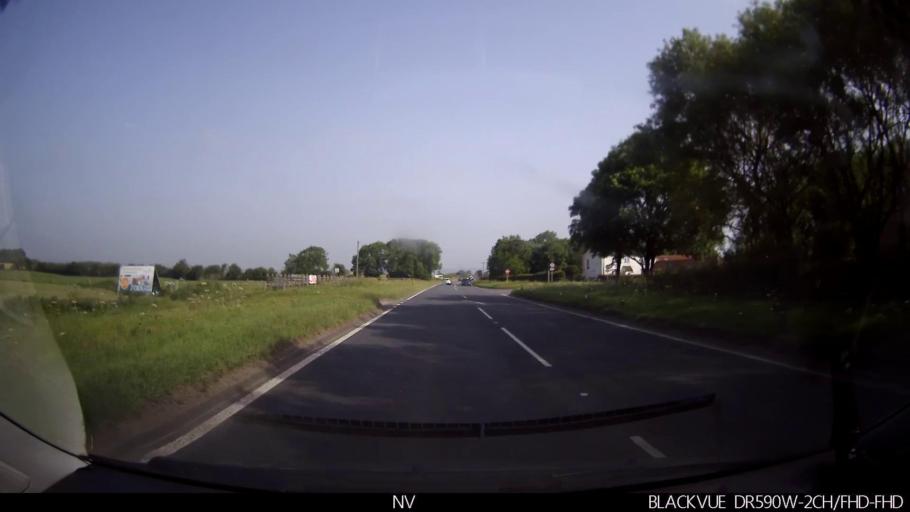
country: GB
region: England
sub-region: North Yorkshire
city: East Ayton
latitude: 54.2152
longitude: -0.4380
